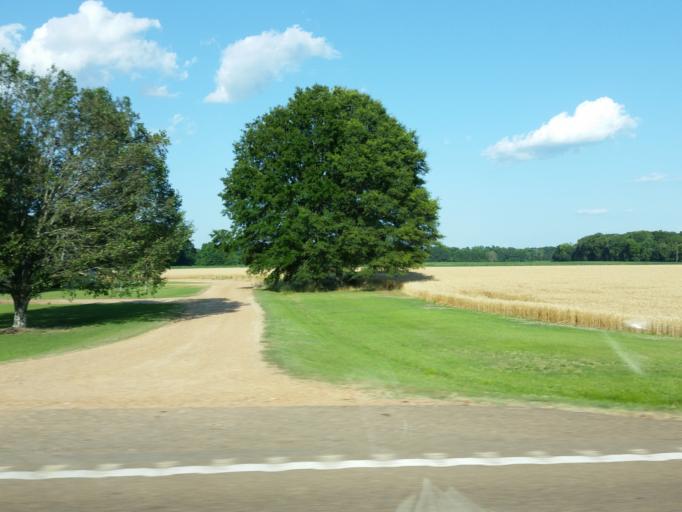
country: US
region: Mississippi
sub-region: Calhoun County
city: Calhoun City
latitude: 33.7645
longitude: -89.3637
